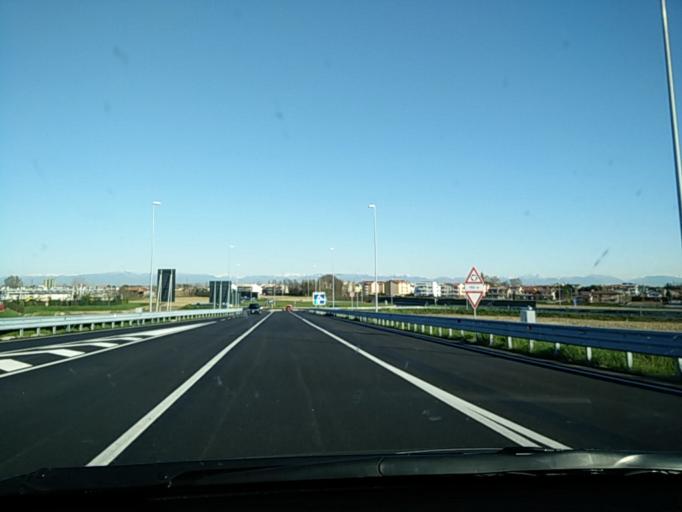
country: IT
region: Veneto
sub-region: Provincia di Venezia
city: Marcon-Gaggio-Colmello
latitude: 45.5473
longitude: 12.2980
